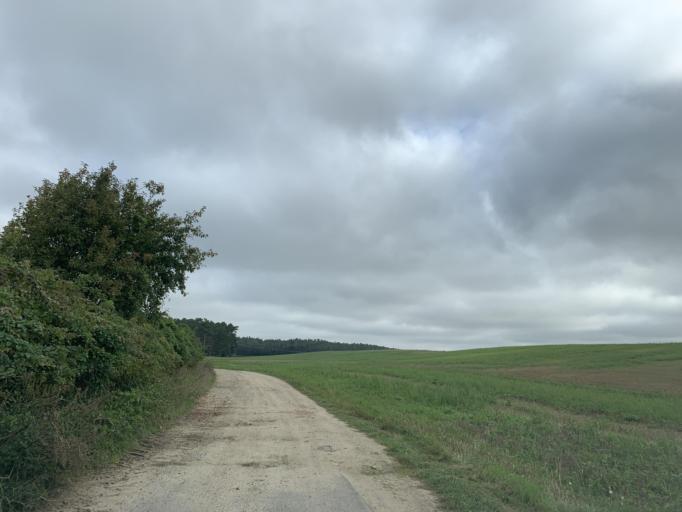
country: DE
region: Mecklenburg-Vorpommern
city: Blankensee
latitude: 53.4204
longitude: 13.2412
